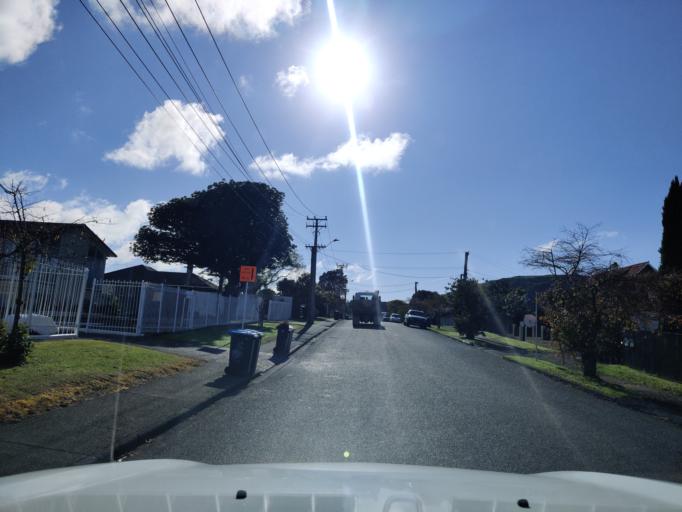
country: NZ
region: Auckland
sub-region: Auckland
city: Tamaki
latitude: -36.8980
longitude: 174.8398
